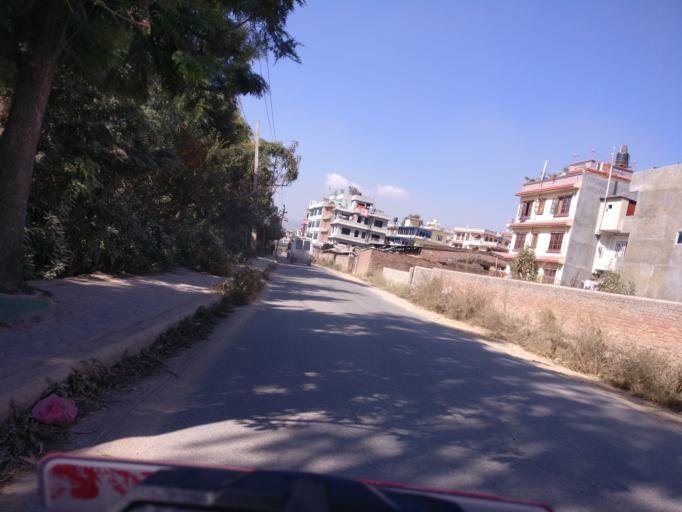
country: NP
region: Central Region
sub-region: Bagmati Zone
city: Patan
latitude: 27.6746
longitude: 85.3405
